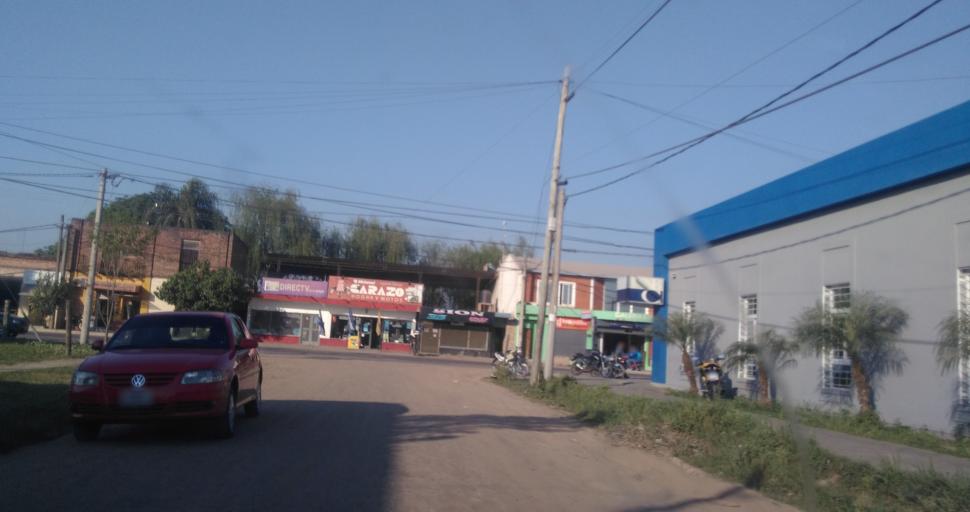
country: AR
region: Chaco
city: Fontana
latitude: -27.4176
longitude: -59.0382
